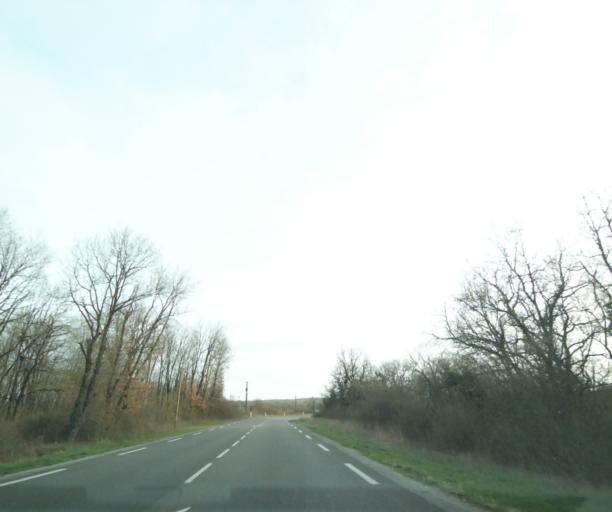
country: FR
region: Midi-Pyrenees
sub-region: Departement du Lot
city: Souillac
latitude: 44.9711
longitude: 1.5051
